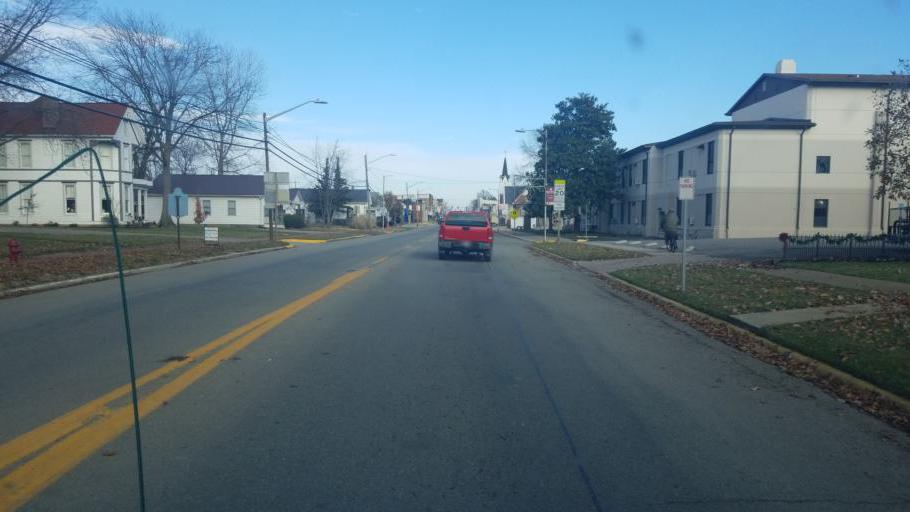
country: US
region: Illinois
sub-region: White County
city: Carmi
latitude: 38.0878
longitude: -88.1638
